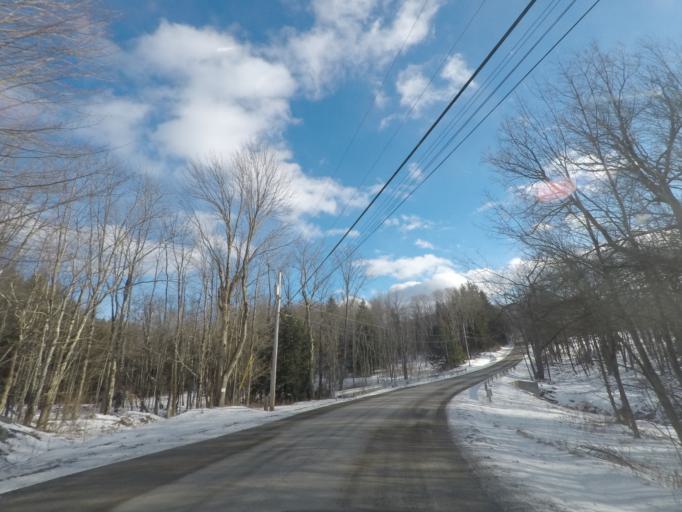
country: US
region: New York
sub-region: Rensselaer County
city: Poestenkill
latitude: 42.7567
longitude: -73.4885
